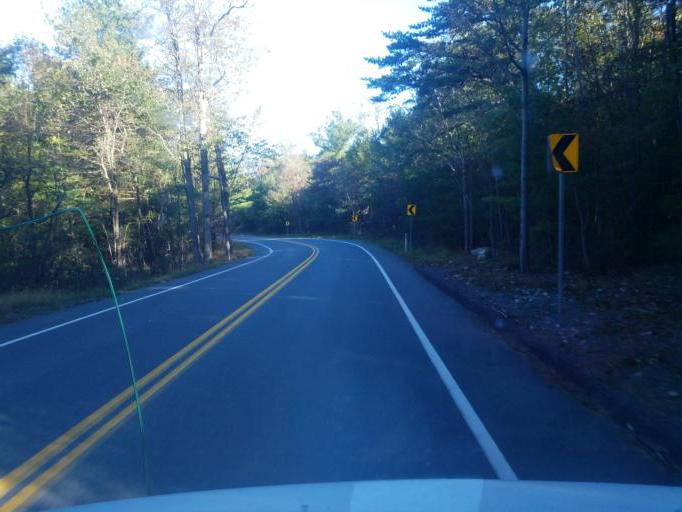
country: US
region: Pennsylvania
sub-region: Franklin County
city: Mont Alto
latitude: 39.8469
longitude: -77.5170
